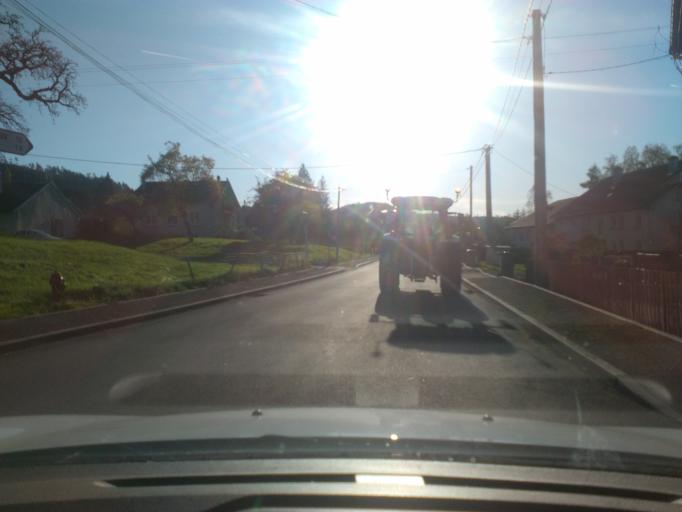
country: FR
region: Lorraine
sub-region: Departement des Vosges
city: Etival-Clairefontaine
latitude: 48.3120
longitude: 6.8265
